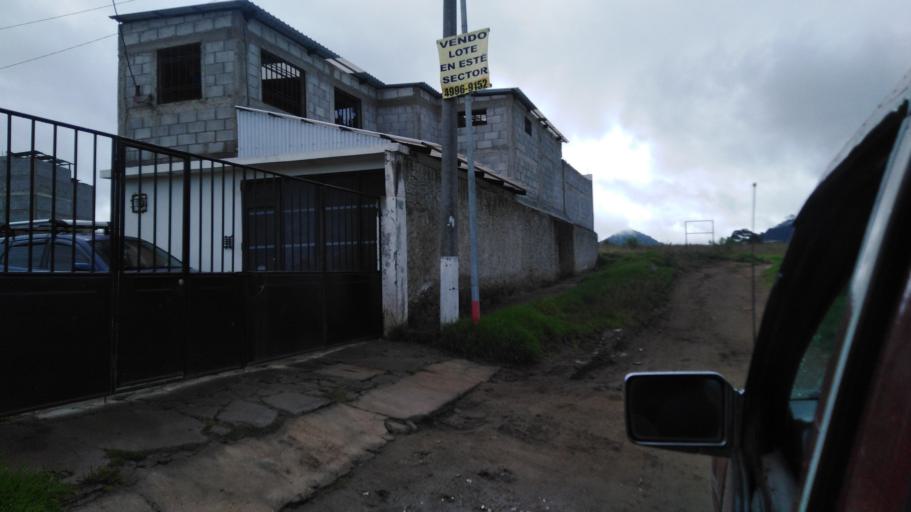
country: GT
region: Quetzaltenango
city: Quetzaltenango
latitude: 14.8526
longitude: -91.5056
